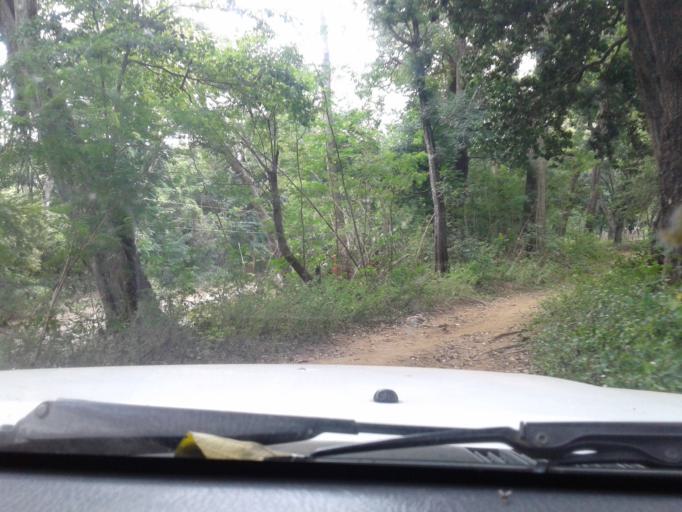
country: NI
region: Rivas
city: San Juan del Sur
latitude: 11.2244
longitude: -85.7858
